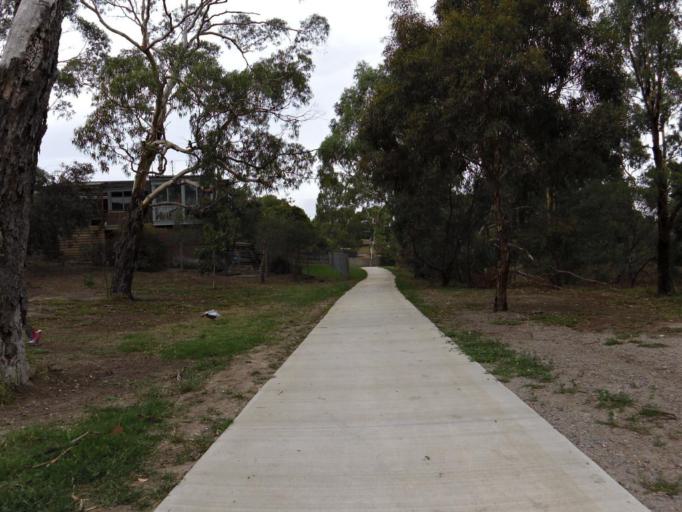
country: AU
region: Victoria
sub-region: Hume
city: Sunbury
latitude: -37.5608
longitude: 144.7239
